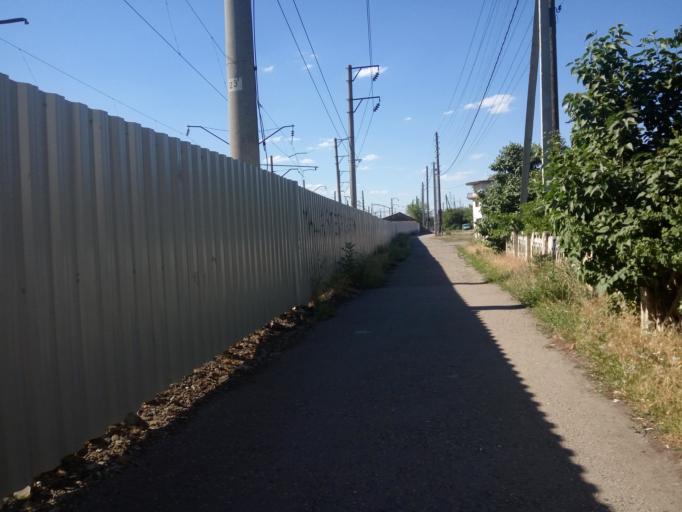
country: RU
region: Rostov
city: Bataysk
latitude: 47.1378
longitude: 39.7587
